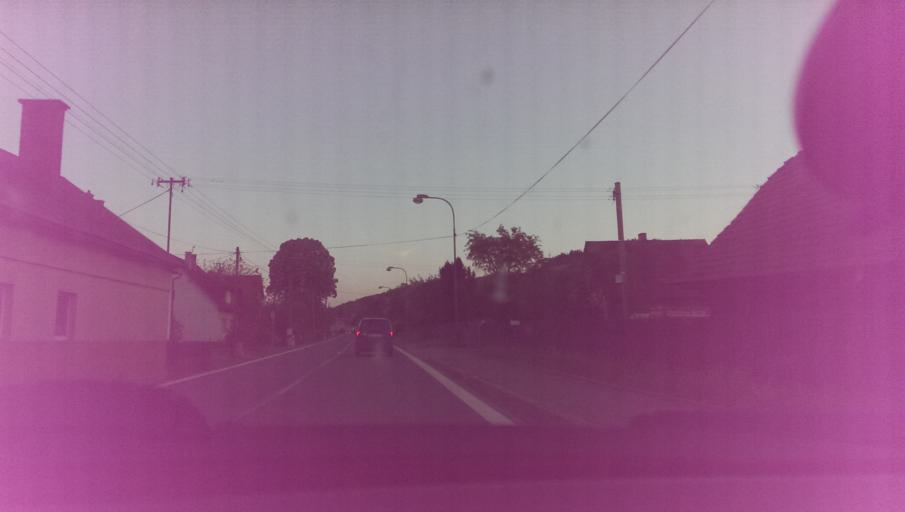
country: CZ
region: Zlin
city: Valasska Polanka
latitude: 49.2900
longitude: 17.9989
